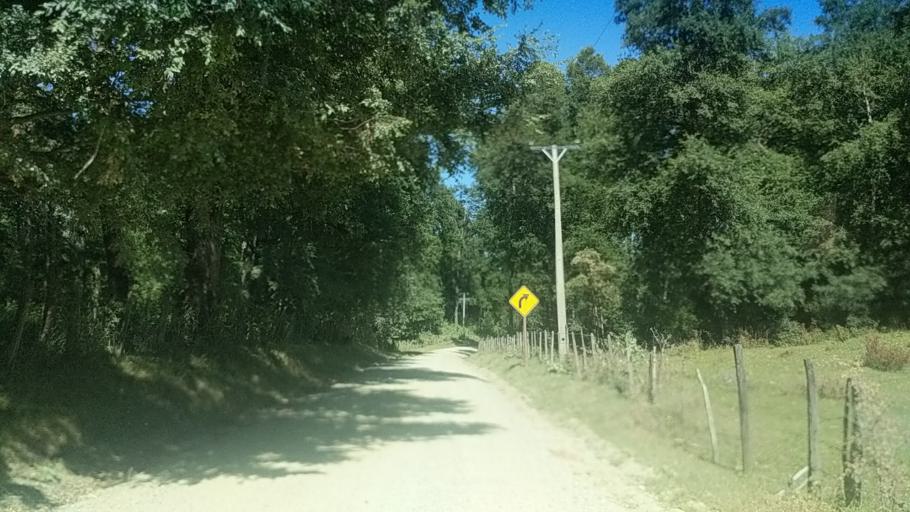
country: CL
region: Araucania
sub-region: Provincia de Cautin
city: Pucon
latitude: -39.0650
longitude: -71.7366
